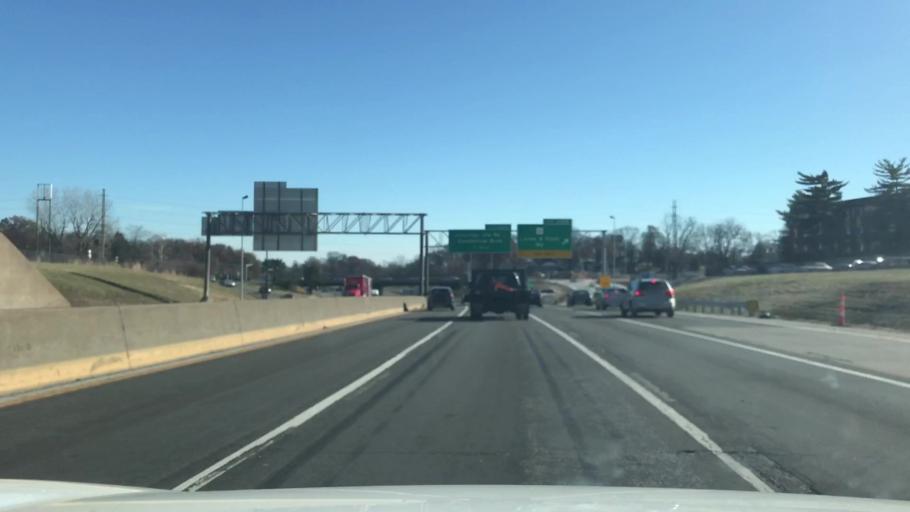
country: US
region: Missouri
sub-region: Saint Louis County
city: Northwoods
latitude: 38.7126
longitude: -90.2888
